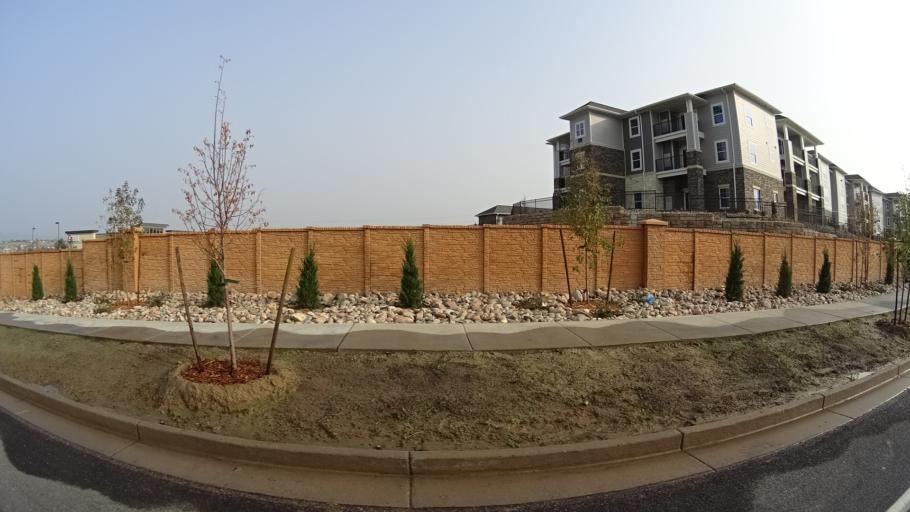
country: US
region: Colorado
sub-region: El Paso County
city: Black Forest
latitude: 38.9376
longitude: -104.7281
